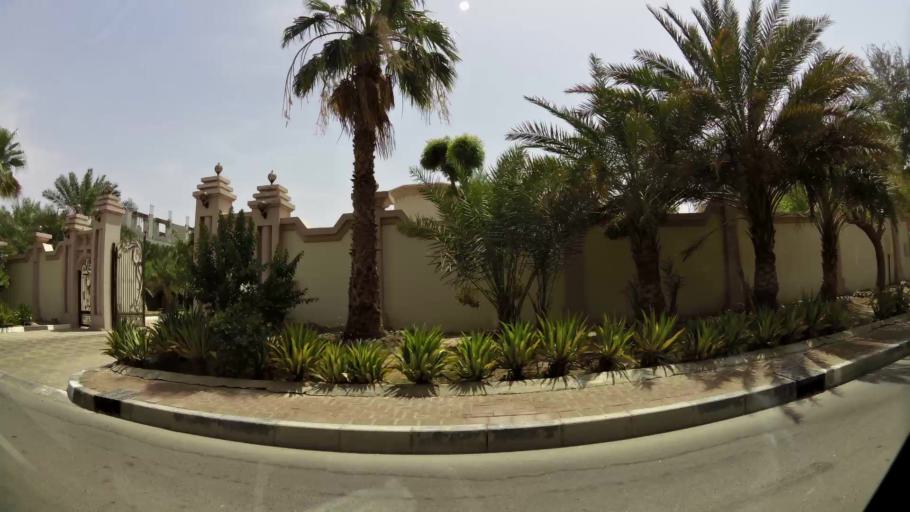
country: AE
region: Abu Dhabi
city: Al Ain
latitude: 24.1778
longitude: 55.7138
